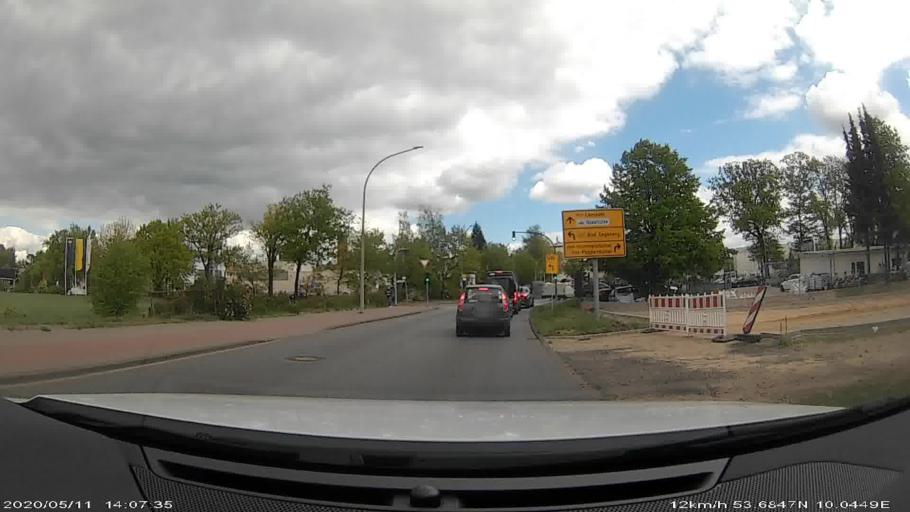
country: DE
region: Hamburg
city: Poppenbuettel
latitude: 53.6840
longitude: 10.0629
